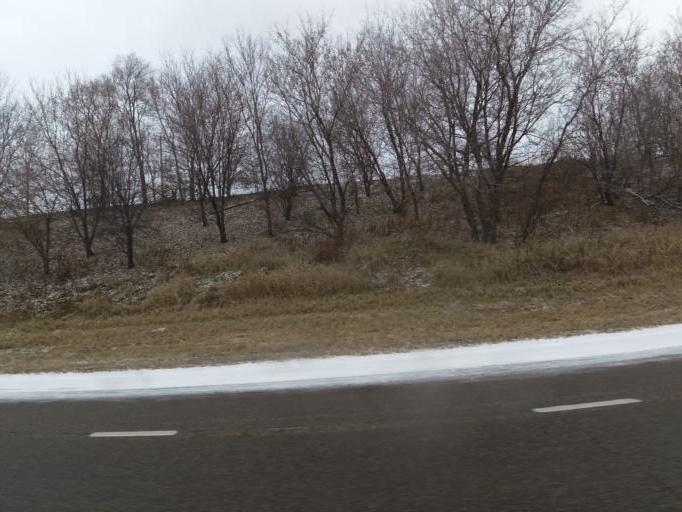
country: US
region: Minnesota
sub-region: Dakota County
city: Eagan
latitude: 44.8103
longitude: -93.2194
